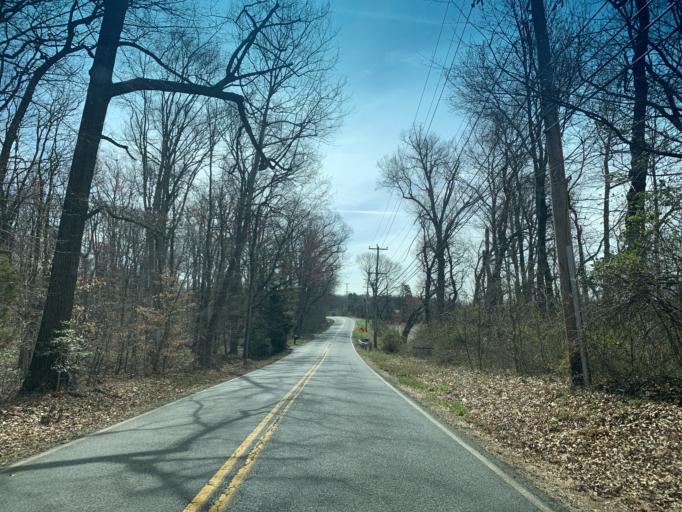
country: US
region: Maryland
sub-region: Cecil County
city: Charlestown
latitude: 39.5624
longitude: -76.0203
